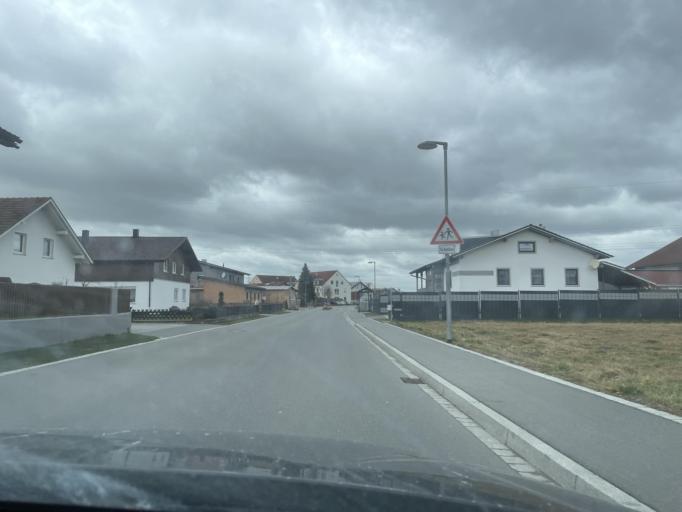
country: DE
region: Bavaria
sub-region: Upper Palatinate
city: Cham
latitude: 49.1983
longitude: 12.6803
